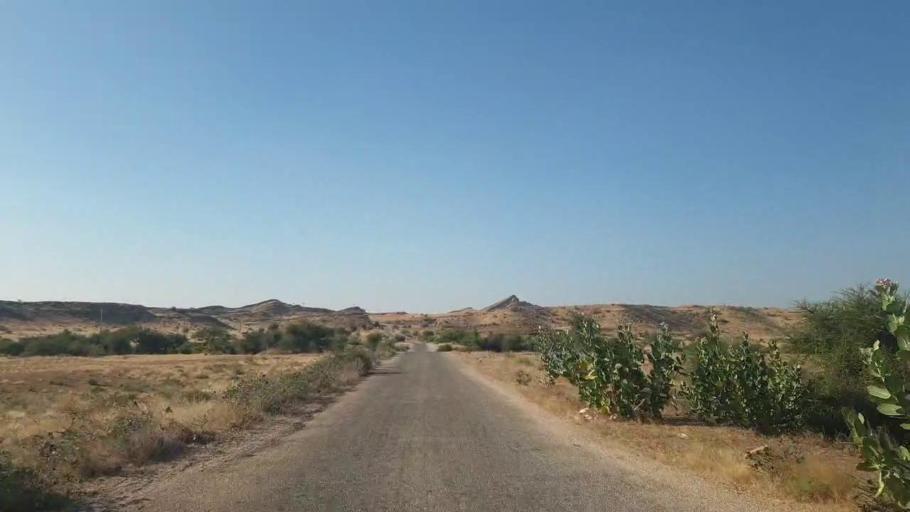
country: PK
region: Sindh
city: Malir Cantonment
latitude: 25.3999
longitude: 67.4907
